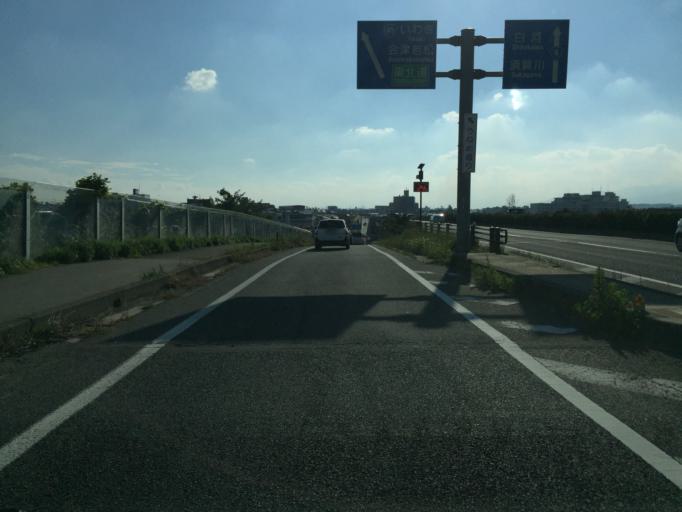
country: JP
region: Fukushima
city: Koriyama
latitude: 37.4139
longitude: 140.3487
